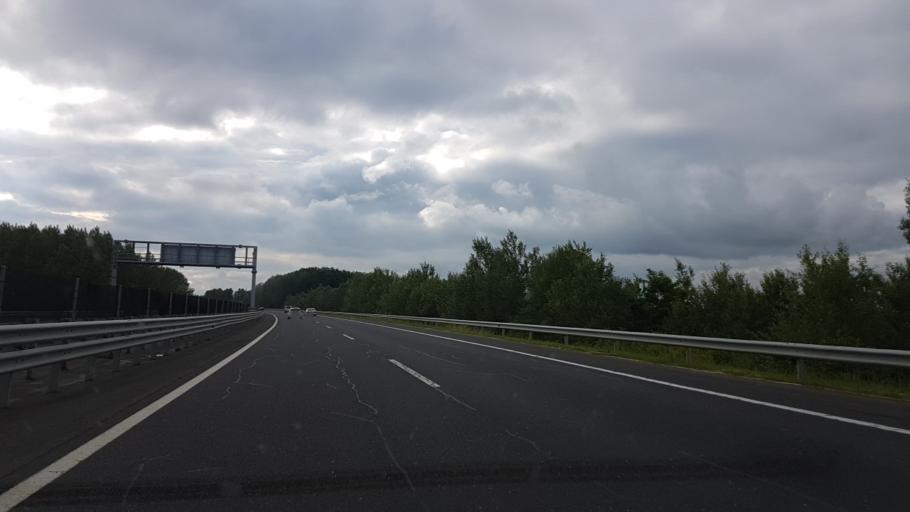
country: HU
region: Hajdu-Bihar
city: Polgar
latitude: 47.8615
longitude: 21.0438
